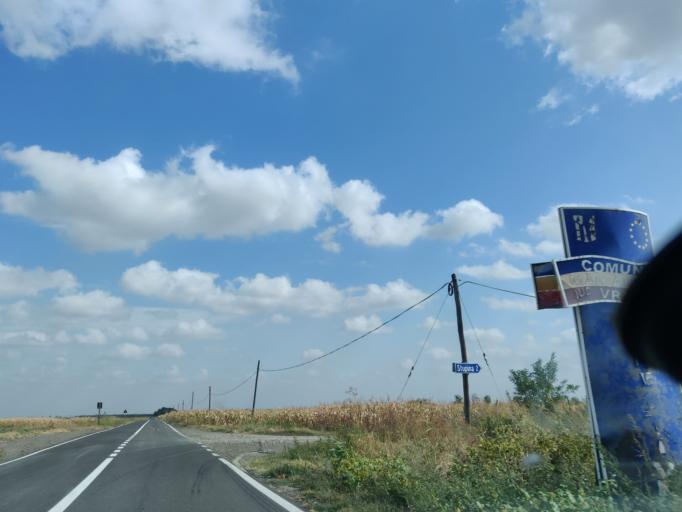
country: RO
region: Vrancea
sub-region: Comuna Maicanesti
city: Ramniceni
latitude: 45.4700
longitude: 27.4263
